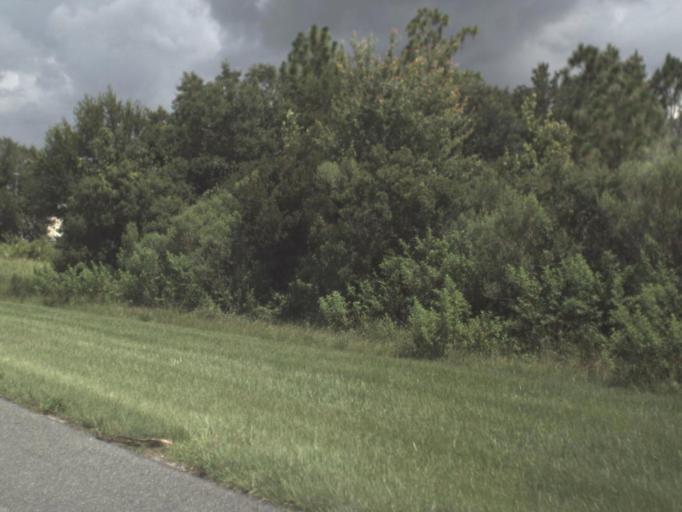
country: US
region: Florida
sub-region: Pasco County
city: Wesley Chapel
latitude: 28.2239
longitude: -82.2802
